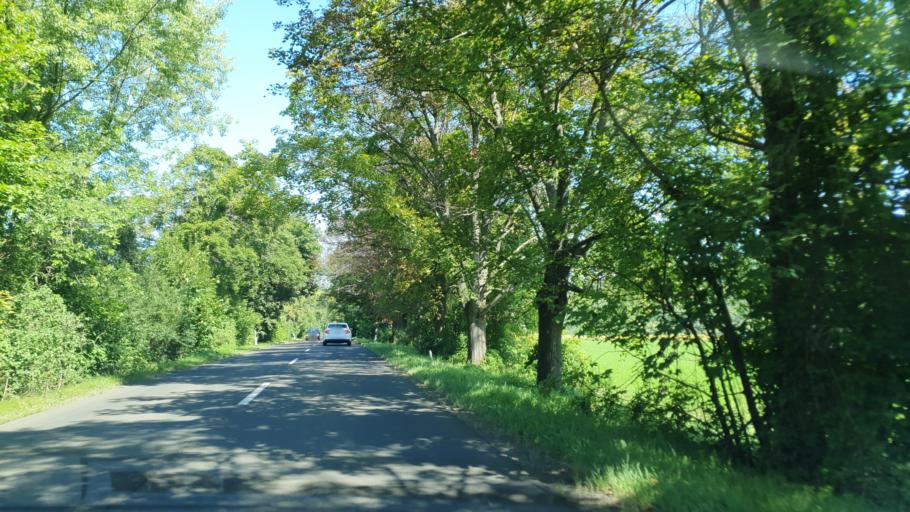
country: HU
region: Nograd
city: Rimoc
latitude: 48.0645
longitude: 19.5568
